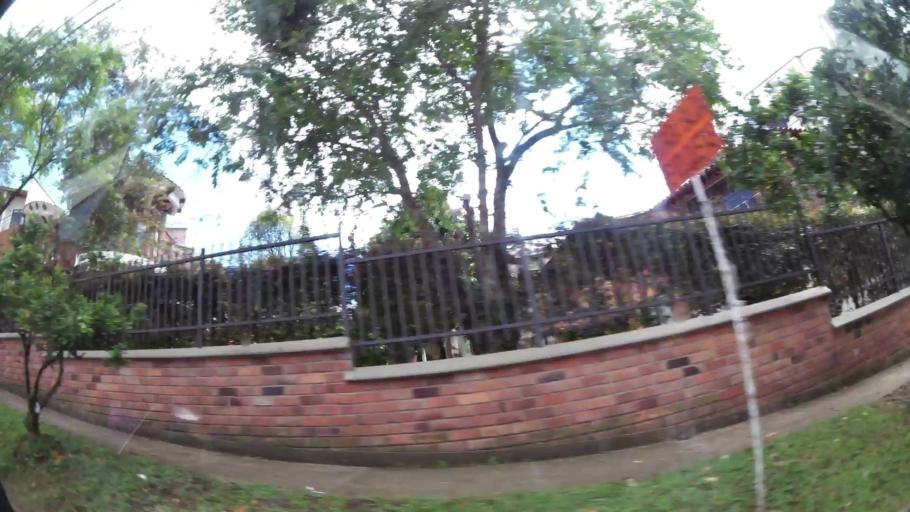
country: CO
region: Antioquia
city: Sabaneta
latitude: 6.1432
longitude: -75.6179
